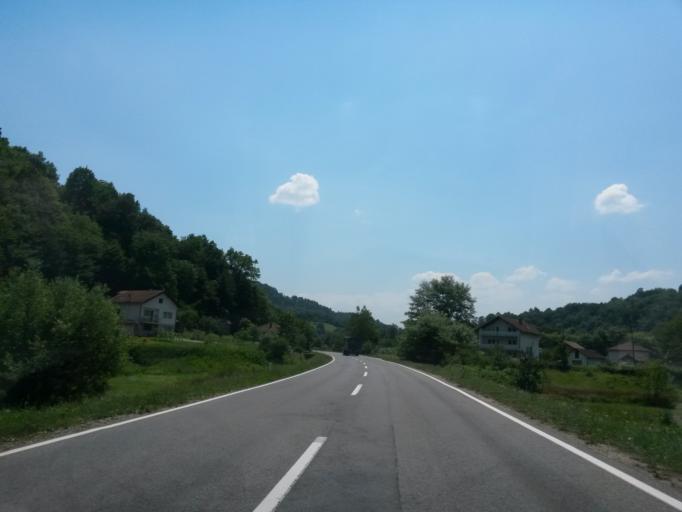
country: BA
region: Federation of Bosnia and Herzegovina
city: Lijesnica
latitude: 44.5125
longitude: 18.0809
